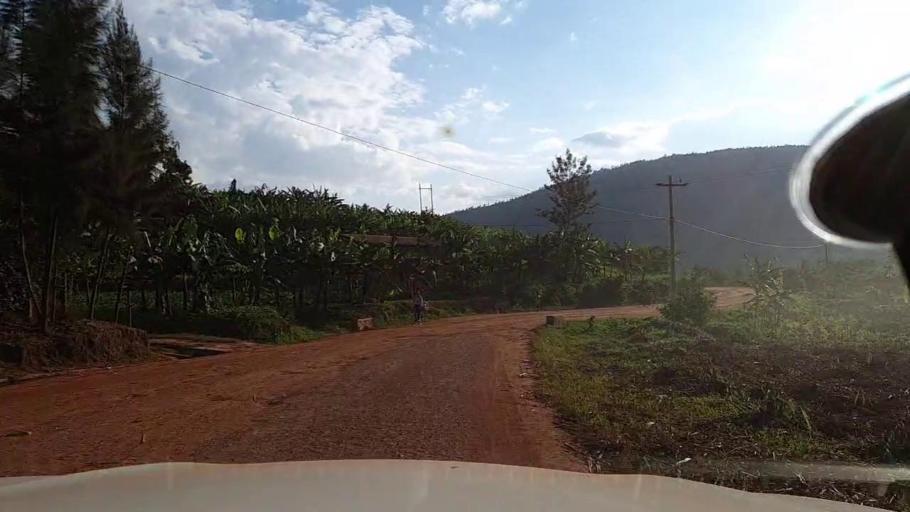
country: RW
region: Kigali
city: Kigali
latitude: -1.9196
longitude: 29.9904
